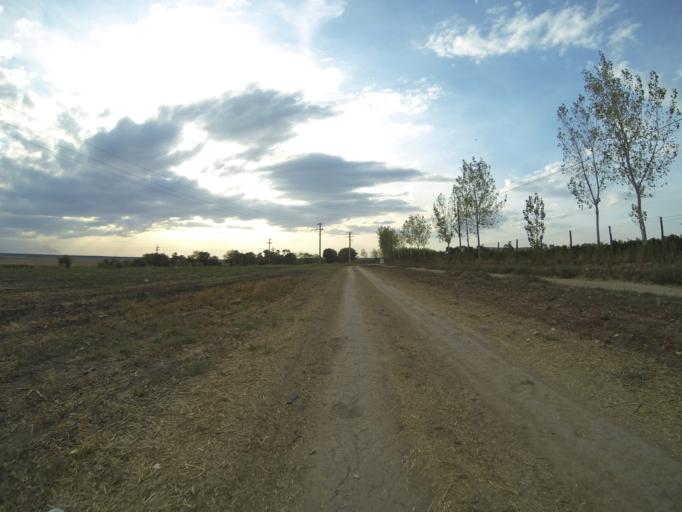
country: RO
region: Dolj
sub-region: Comuna Segarcea
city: Segarcea
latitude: 44.1008
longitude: 23.7233
